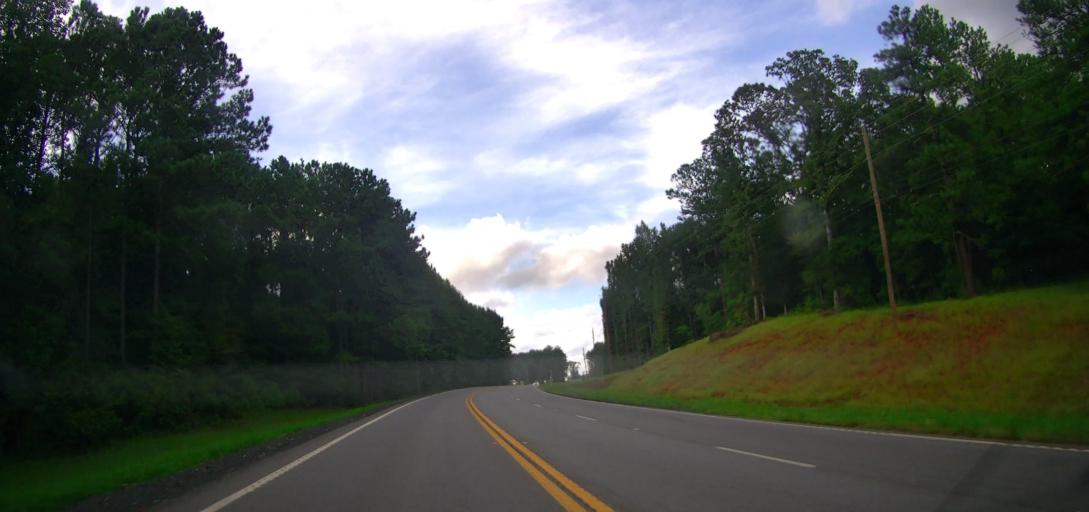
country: US
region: Georgia
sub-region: Harris County
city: Hamilton
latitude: 32.7120
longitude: -84.8719
